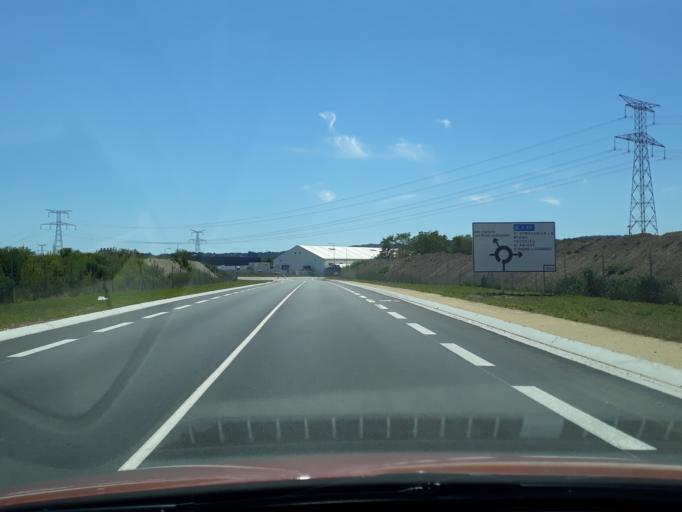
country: FR
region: Rhone-Alpes
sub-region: Departement du Rhone
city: Toussieu
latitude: 45.6665
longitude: 5.0021
